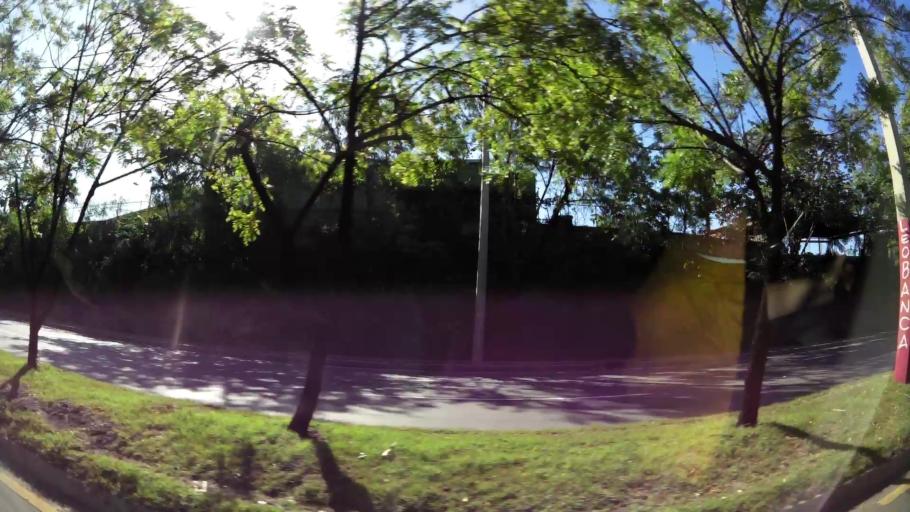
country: DO
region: Nacional
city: Bella Vista
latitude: 18.4521
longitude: -69.9846
